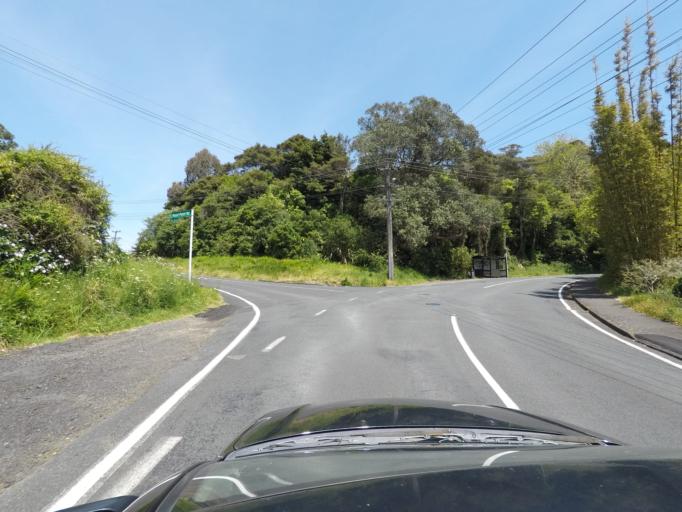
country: NZ
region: Auckland
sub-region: Auckland
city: Titirangi
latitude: -36.9696
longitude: 174.6358
